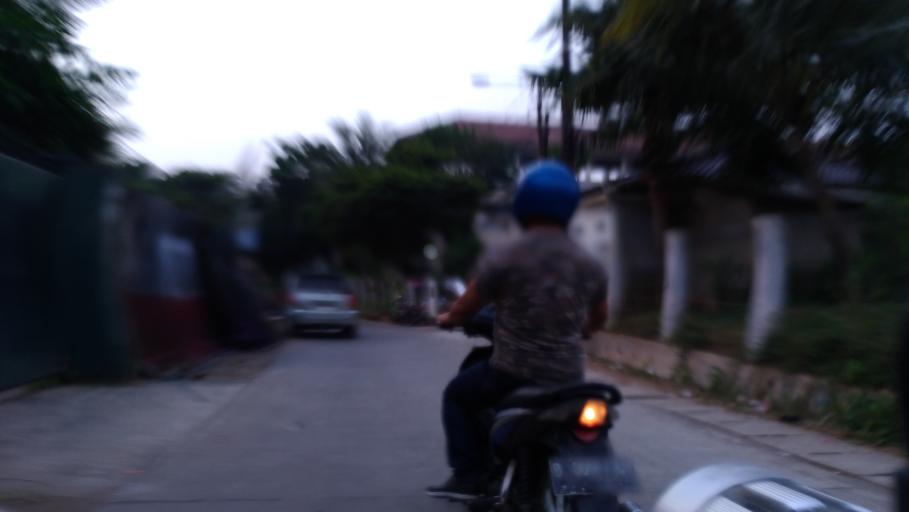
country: ID
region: West Java
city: Depok
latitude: -6.3586
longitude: 106.8704
